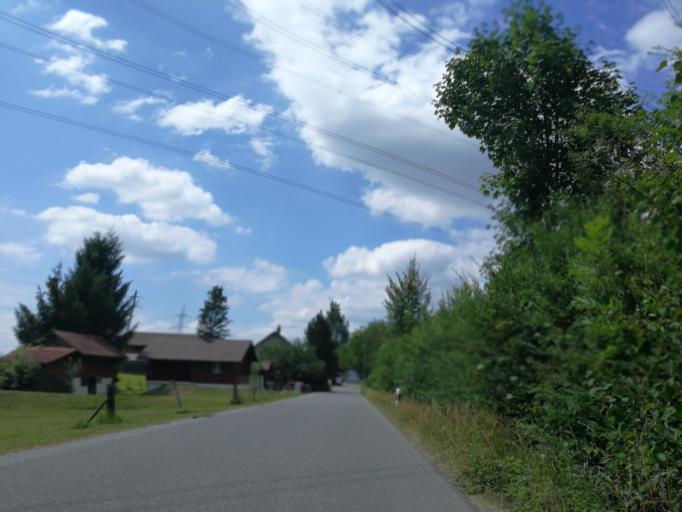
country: CH
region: Saint Gallen
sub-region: Wahlkreis See-Gaster
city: Benken
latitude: 47.1813
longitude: 8.9987
